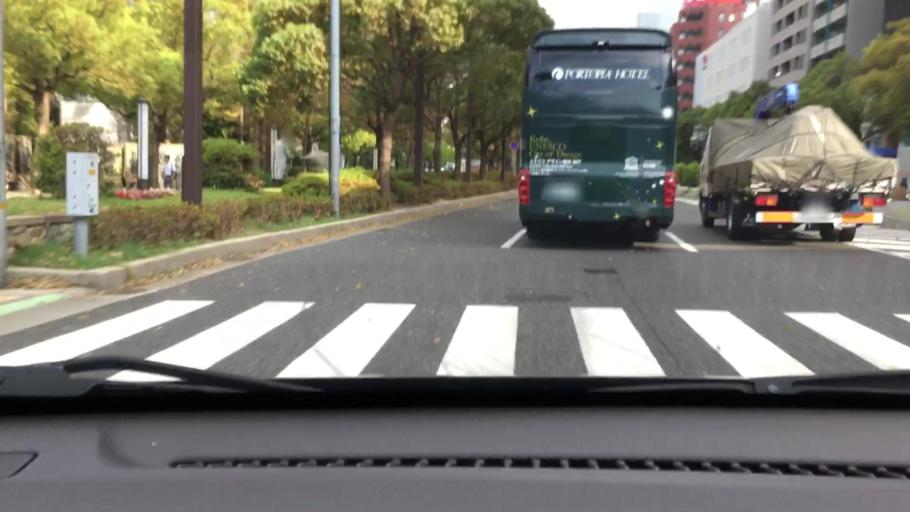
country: JP
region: Hyogo
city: Kobe
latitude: 34.6877
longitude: 135.1972
